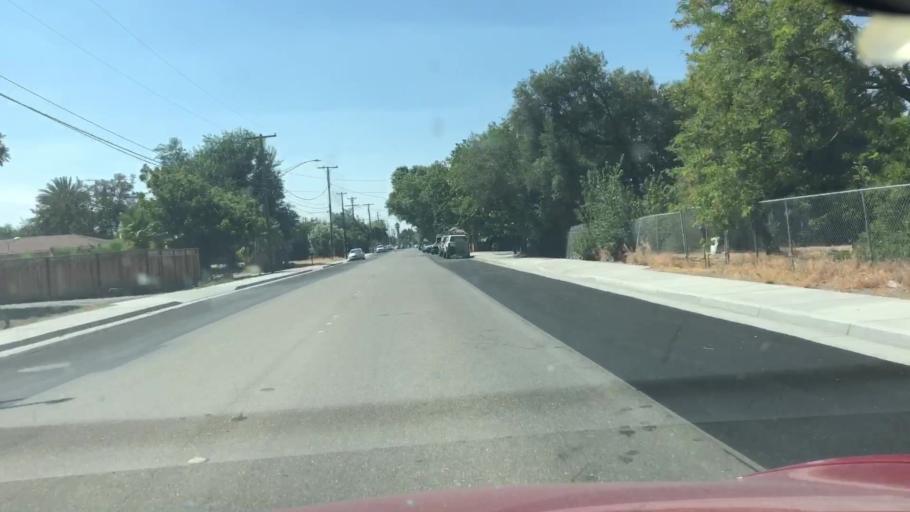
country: US
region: California
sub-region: San Joaquin County
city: Tracy
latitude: 37.7289
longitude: -121.4289
